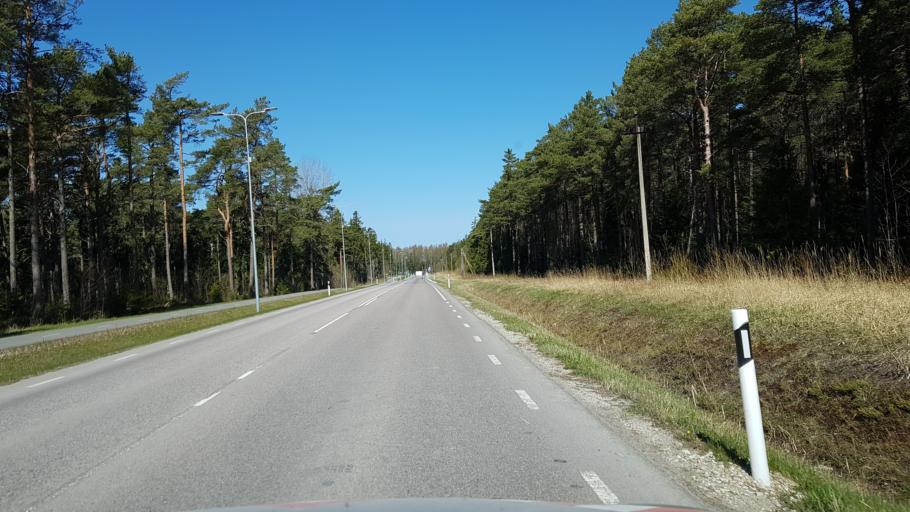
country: EE
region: Harju
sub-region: Viimsi vald
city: Viimsi
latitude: 59.5177
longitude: 24.8992
